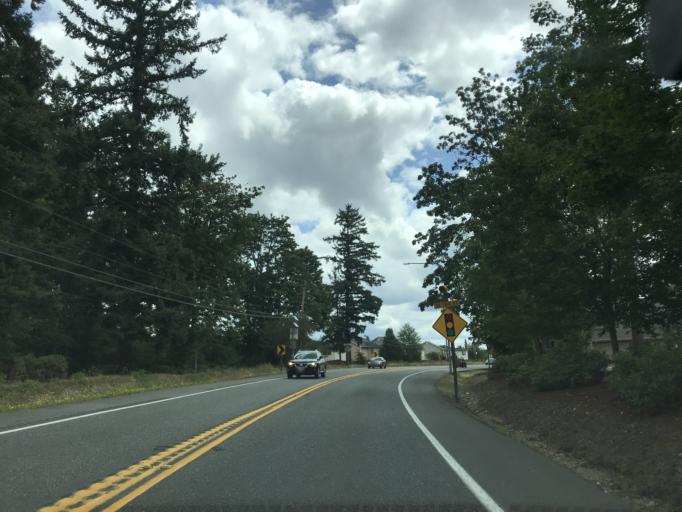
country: US
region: Washington
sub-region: King County
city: Maple Heights-Lake Desire
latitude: 47.4391
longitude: -122.1184
